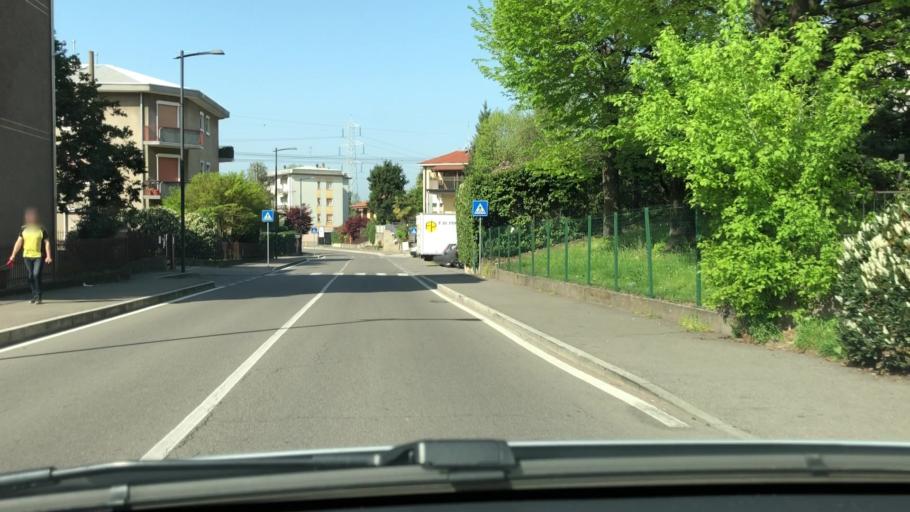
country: IT
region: Lombardy
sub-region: Provincia di Monza e Brianza
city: Barlassina
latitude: 45.6427
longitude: 9.1280
